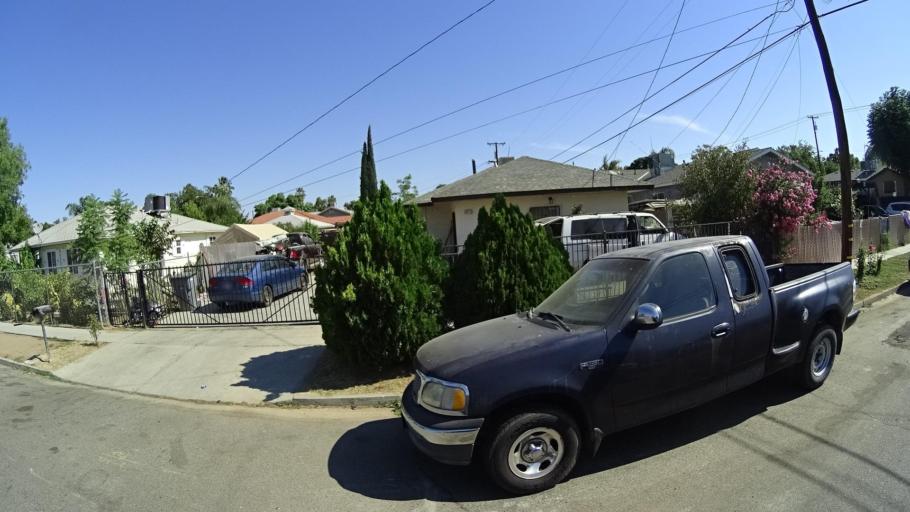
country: US
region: California
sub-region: Fresno County
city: Fresno
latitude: 36.7261
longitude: -119.7666
